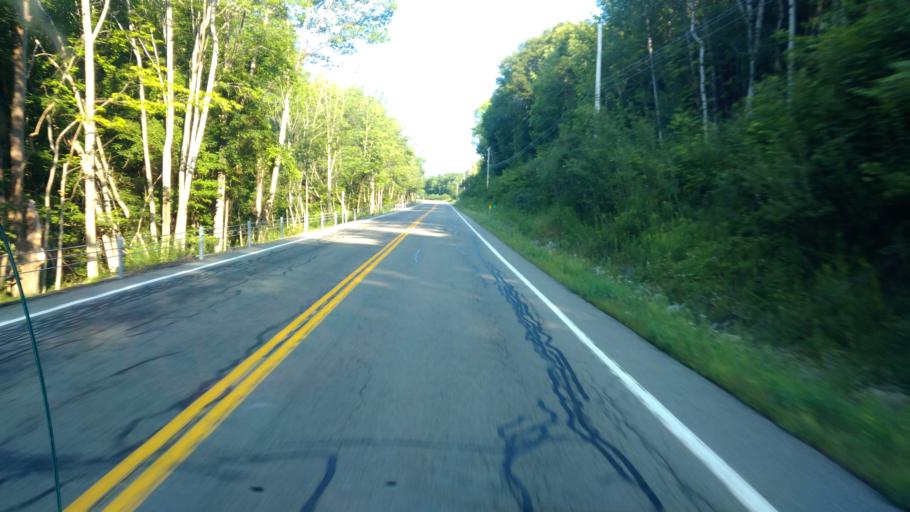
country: US
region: New York
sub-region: Allegany County
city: Andover
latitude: 42.1522
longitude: -77.6949
